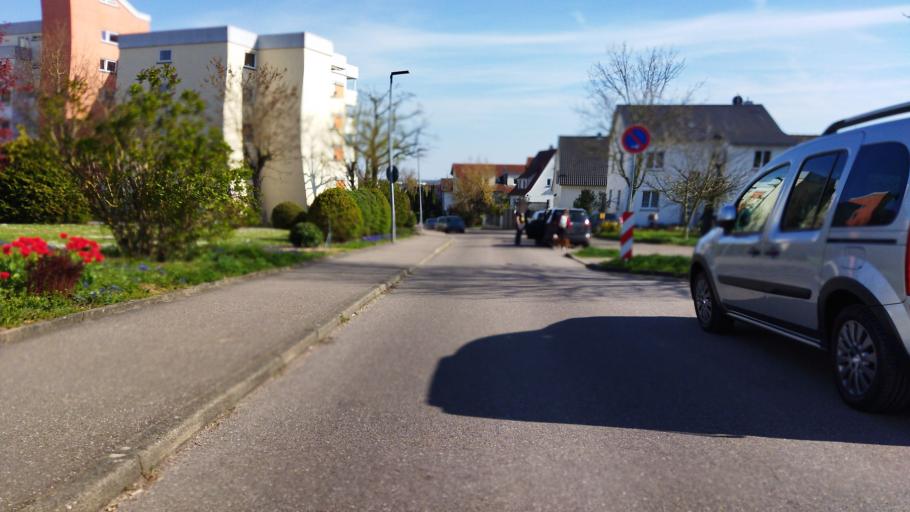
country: DE
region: Baden-Wuerttemberg
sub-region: Regierungsbezirk Stuttgart
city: Freudental
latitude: 48.9724
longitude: 9.0698
